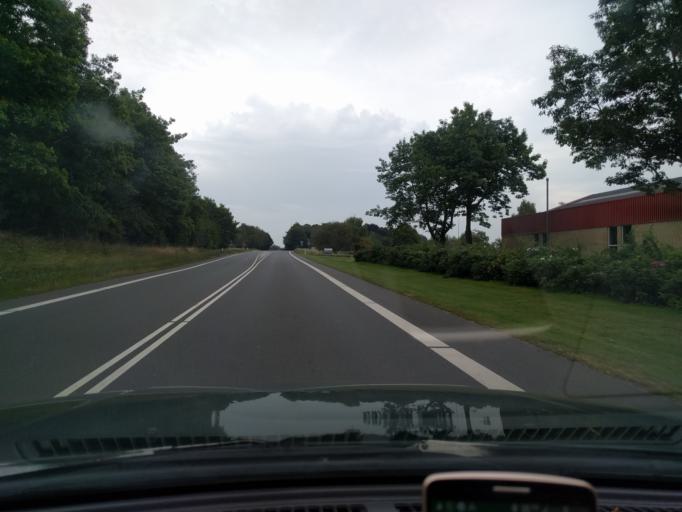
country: DK
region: Zealand
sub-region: Slagelse Kommune
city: Skaelskor
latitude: 55.2547
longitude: 11.3222
